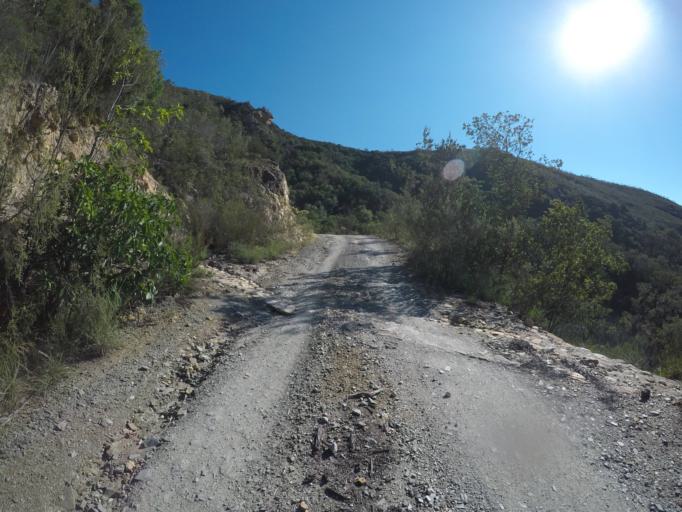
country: ZA
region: Eastern Cape
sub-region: Cacadu District Municipality
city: Kareedouw
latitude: -33.6566
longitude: 24.5055
